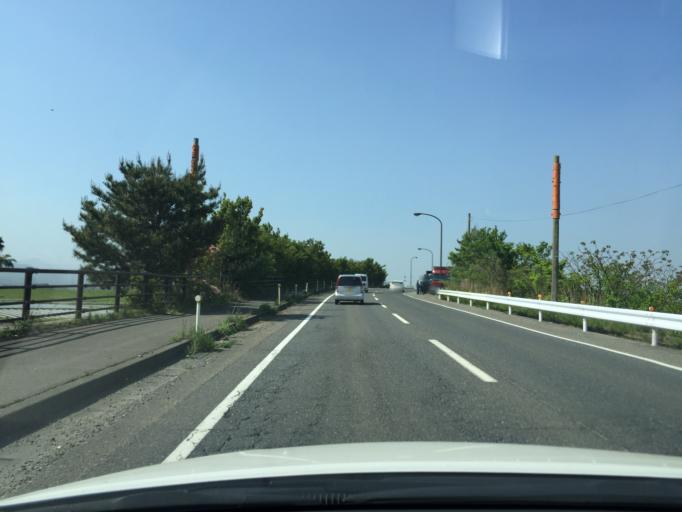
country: JP
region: Niigata
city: Gosen
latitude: 37.7553
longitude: 139.2288
